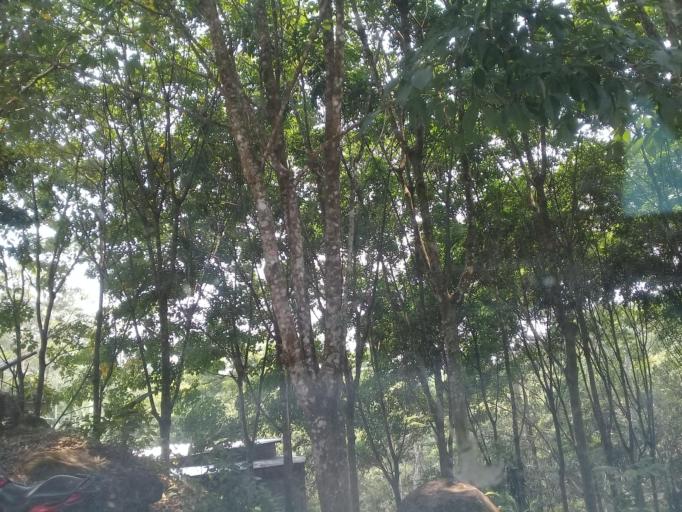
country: MX
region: Veracruz
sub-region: Tezonapa
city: Laguna Chica (Pueblo Nuevo)
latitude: 18.5480
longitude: -96.7363
